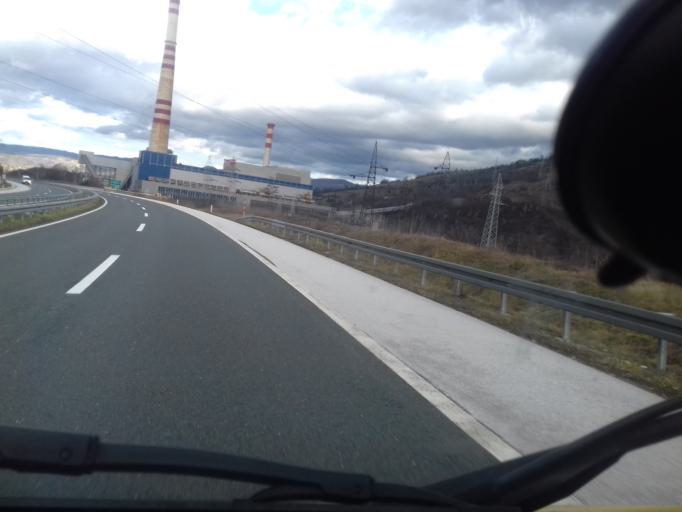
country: BA
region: Federation of Bosnia and Herzegovina
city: Dobrinje
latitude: 44.0829
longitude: 18.1123
